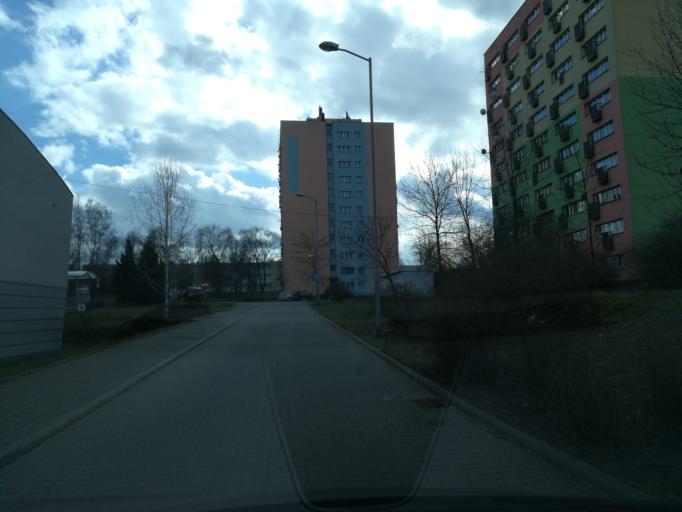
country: PL
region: Silesian Voivodeship
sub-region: Dabrowa Gornicza
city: Dabrowa Gornicza
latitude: 50.3208
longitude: 19.1896
